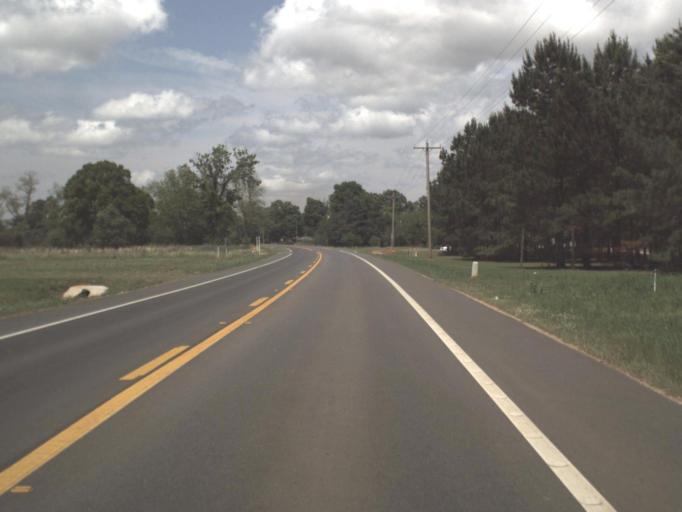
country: US
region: Florida
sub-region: Escambia County
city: Century
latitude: 30.9304
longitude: -87.1578
